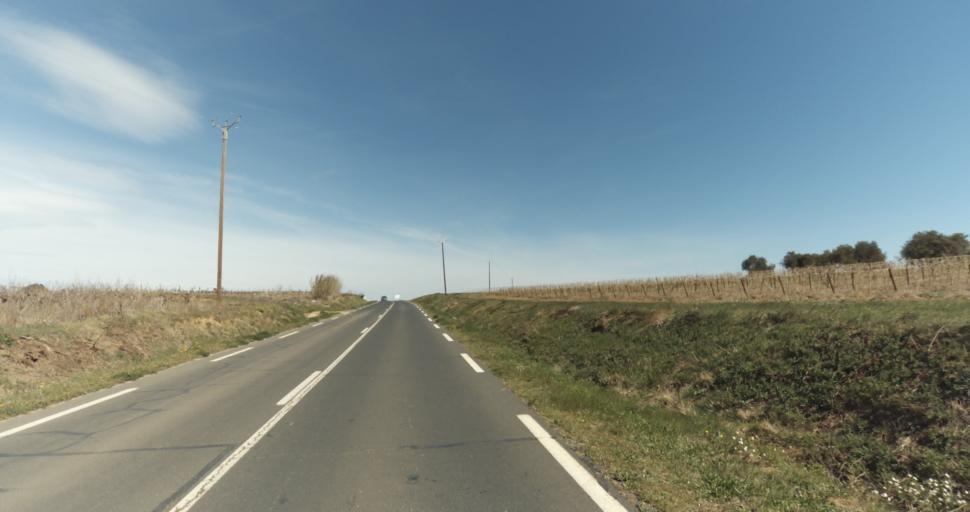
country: FR
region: Languedoc-Roussillon
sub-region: Departement de l'Herault
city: Marseillan
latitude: 43.3719
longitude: 3.5330
